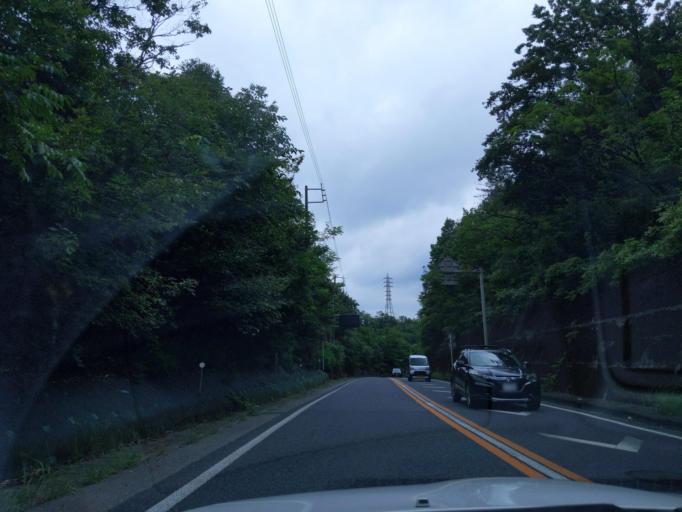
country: JP
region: Aichi
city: Seto
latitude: 35.2128
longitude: 137.1058
